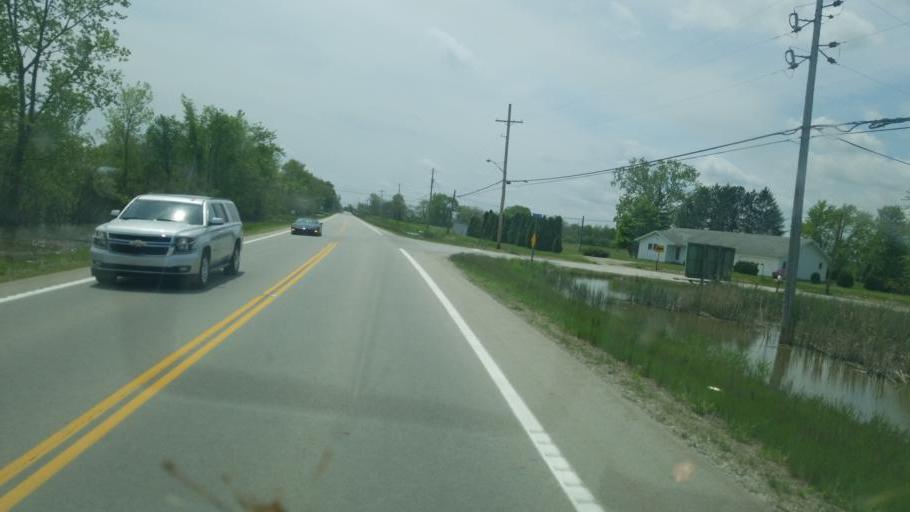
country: US
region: Ohio
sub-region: Ottawa County
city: Oak Harbor
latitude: 41.4622
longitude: -83.0489
